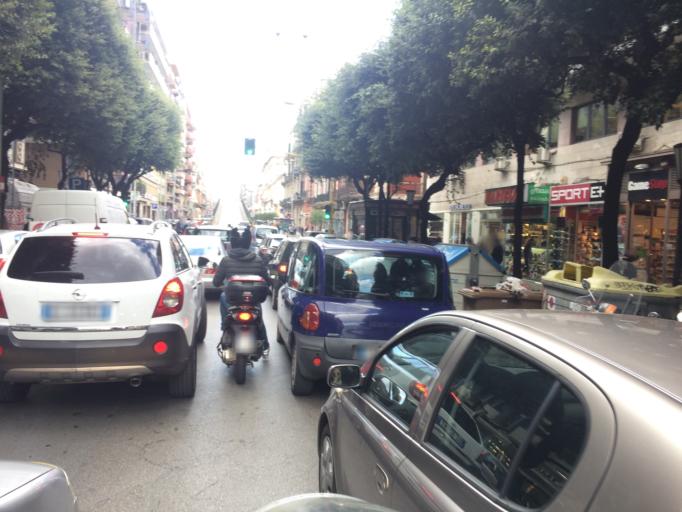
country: IT
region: Apulia
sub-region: Provincia di Bari
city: Bari
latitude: 41.1204
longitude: 16.8726
